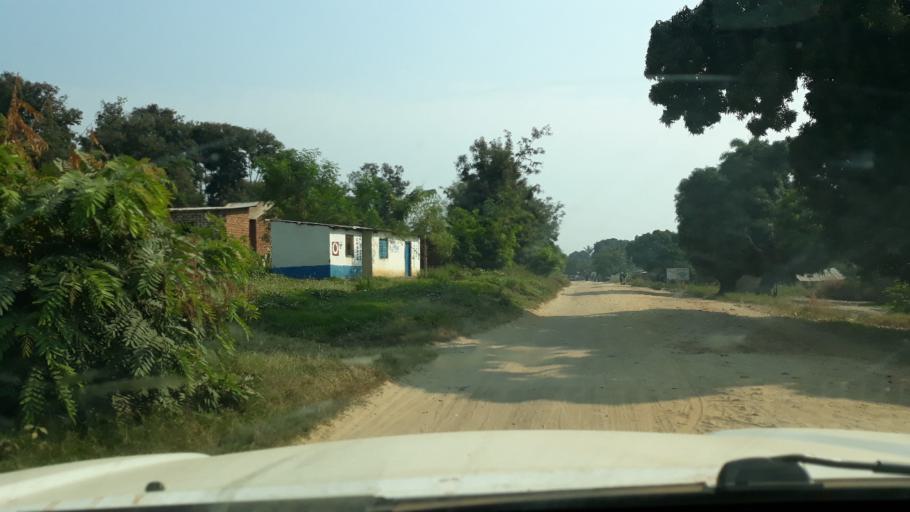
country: BI
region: Bururi
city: Rumonge
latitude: -3.8894
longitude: 29.1016
